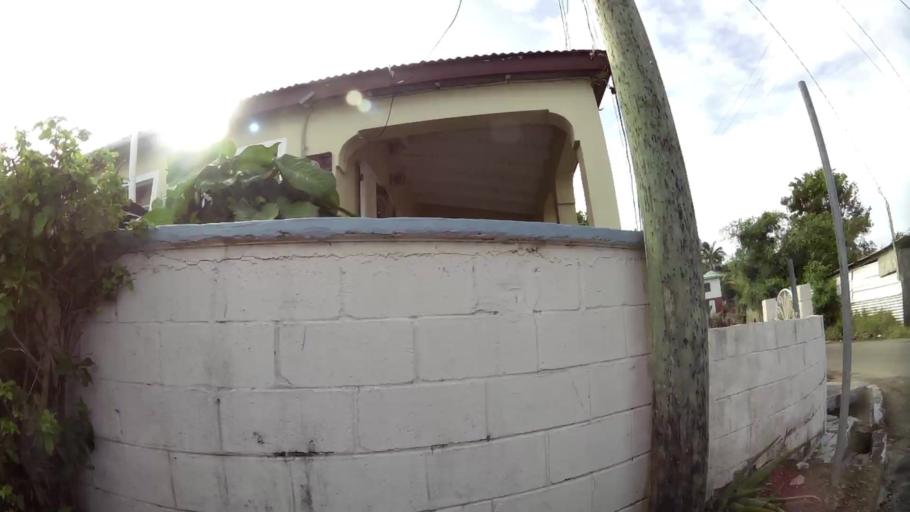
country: AG
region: Saint George
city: Piggotts
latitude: 17.1431
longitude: -61.8081
